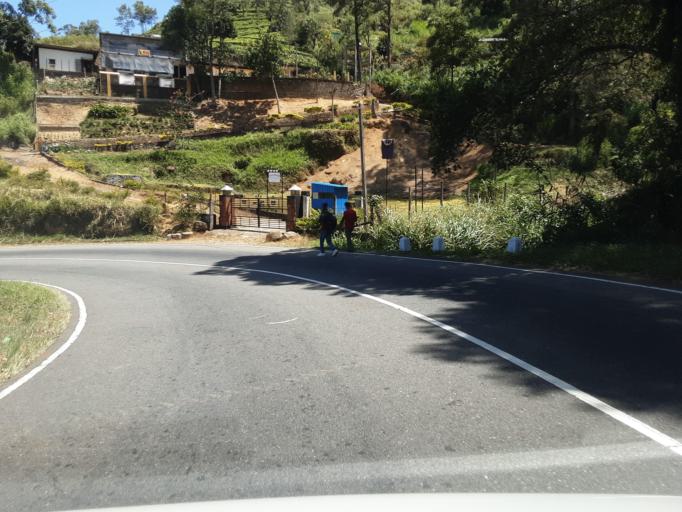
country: LK
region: Uva
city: Haputale
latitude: 6.7652
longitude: 80.9530
